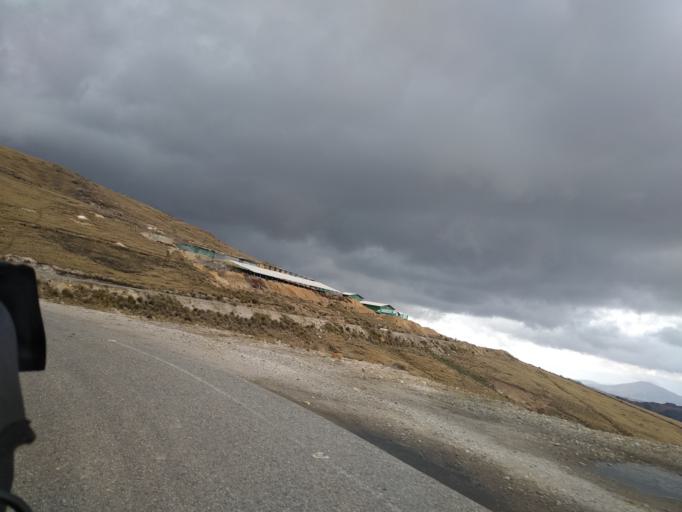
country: PE
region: La Libertad
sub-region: Provincia de Santiago de Chuco
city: Quiruvilca
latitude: -7.9926
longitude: -78.2982
